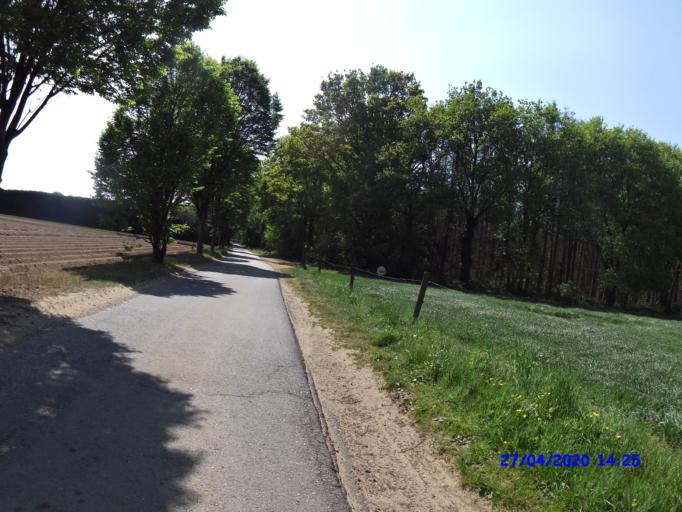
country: BE
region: Flanders
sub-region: Provincie Antwerpen
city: Lille
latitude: 51.2455
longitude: 4.8717
